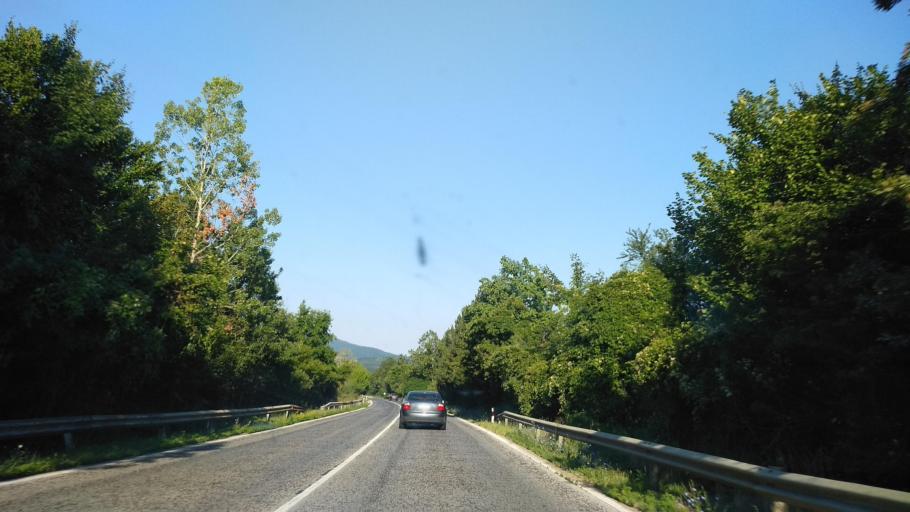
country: BG
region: Lovech
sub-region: Obshtina Lovech
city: Lovech
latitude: 43.0508
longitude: 24.9023
